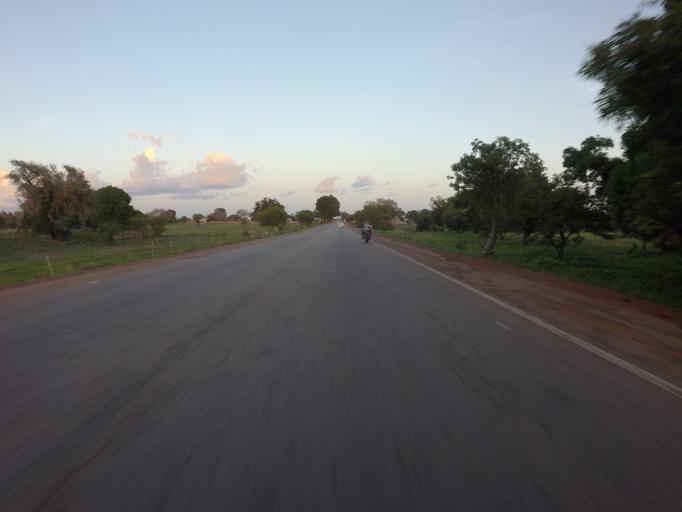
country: GH
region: Upper East
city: Navrongo
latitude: 10.8632
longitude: -1.0351
